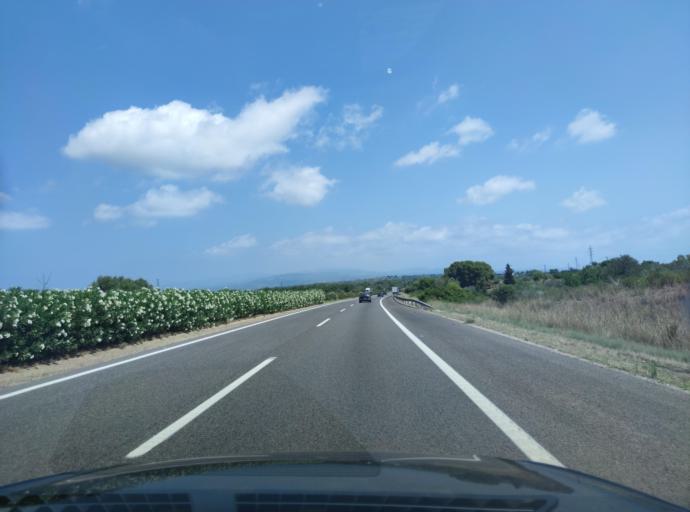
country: ES
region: Catalonia
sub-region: Provincia de Tarragona
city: Masdenverge
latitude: 40.6869
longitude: 0.5268
